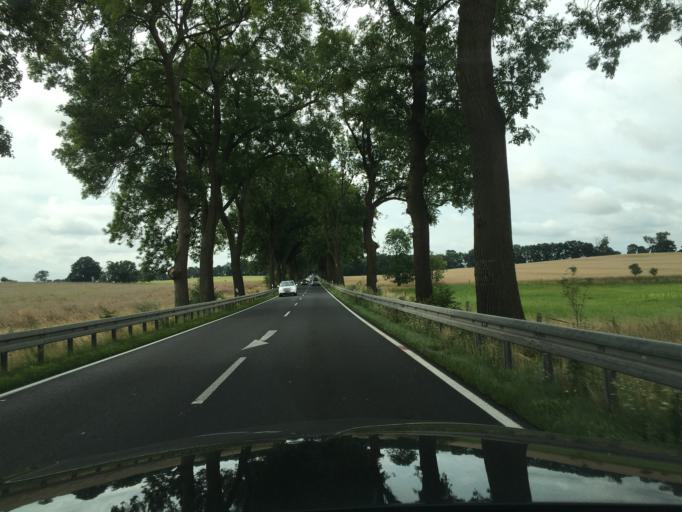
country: DE
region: Brandenburg
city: Gransee
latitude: 52.9583
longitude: 13.1502
